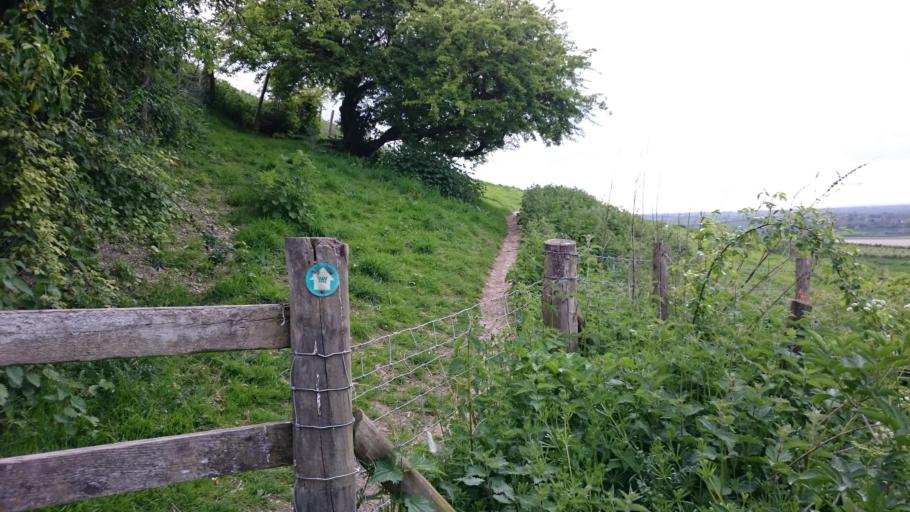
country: GB
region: England
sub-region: Hampshire
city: Kingsclere
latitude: 51.3103
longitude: -1.2303
